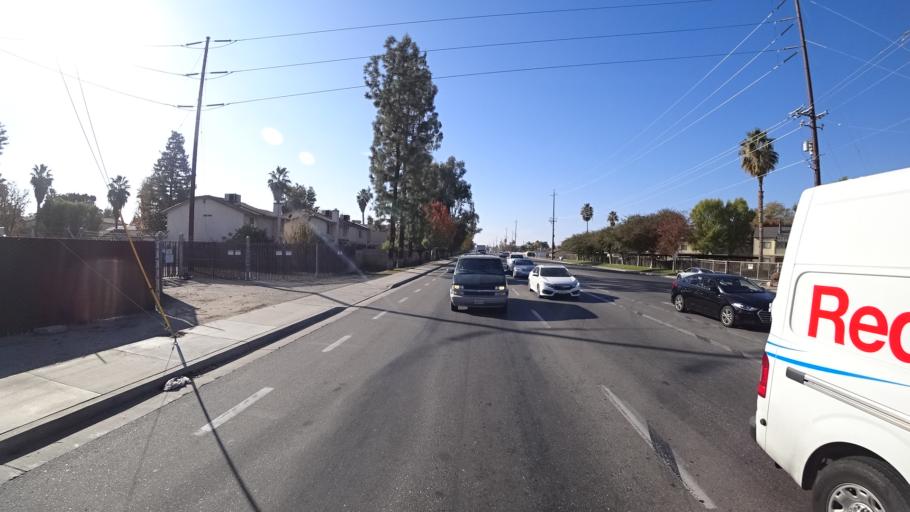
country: US
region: California
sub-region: Kern County
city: Greenfield
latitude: 35.2958
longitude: -119.0217
